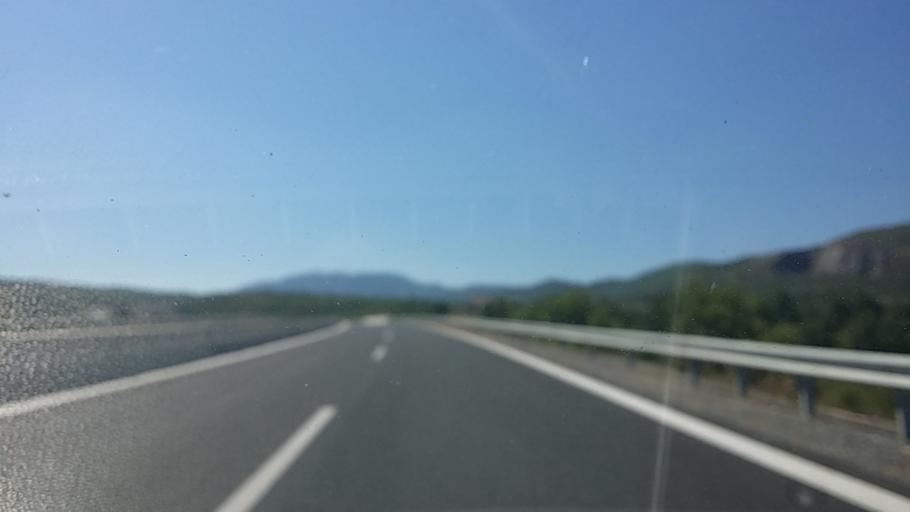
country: GR
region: Peloponnese
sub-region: Nomos Arkadias
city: Megalopoli
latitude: 37.3351
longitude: 22.1534
